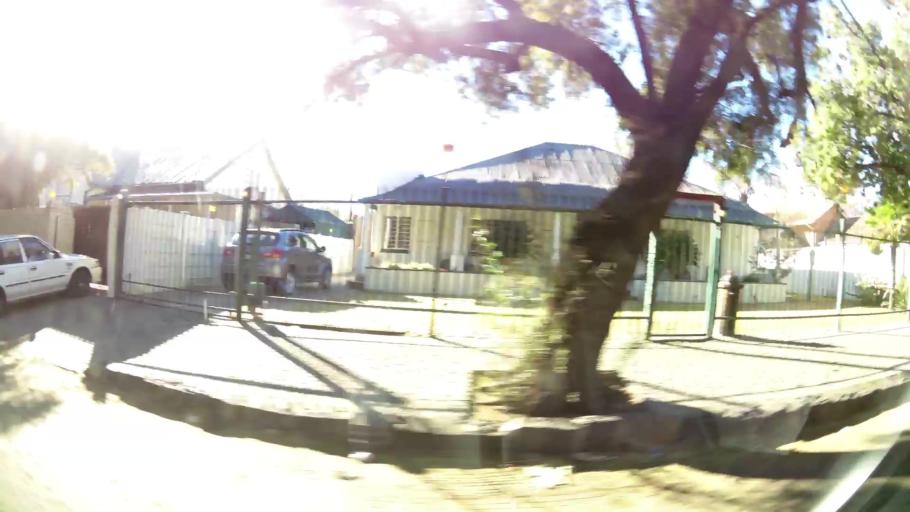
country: ZA
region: Northern Cape
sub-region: Frances Baard District Municipality
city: Kimberley
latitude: -28.7426
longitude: 24.7765
